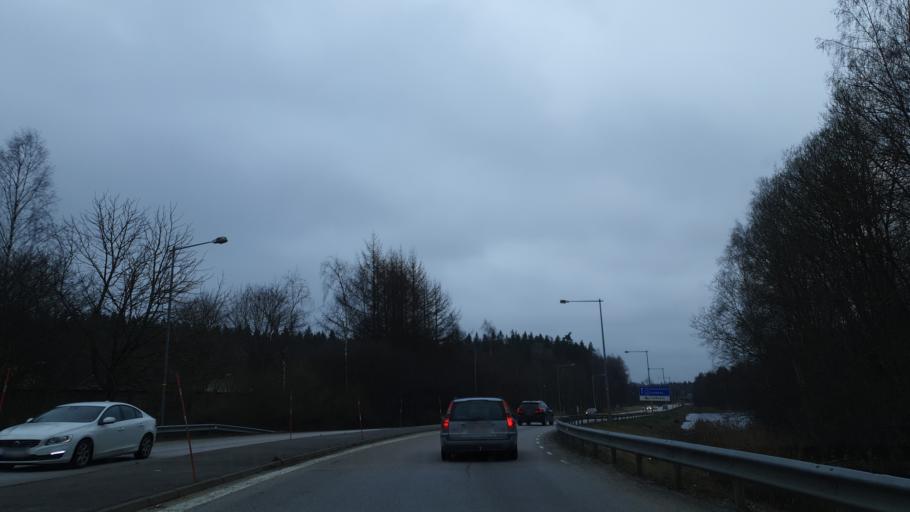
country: SE
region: Vaestra Goetaland
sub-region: Boras Kommun
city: Boras
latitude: 57.6981
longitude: 12.9491
